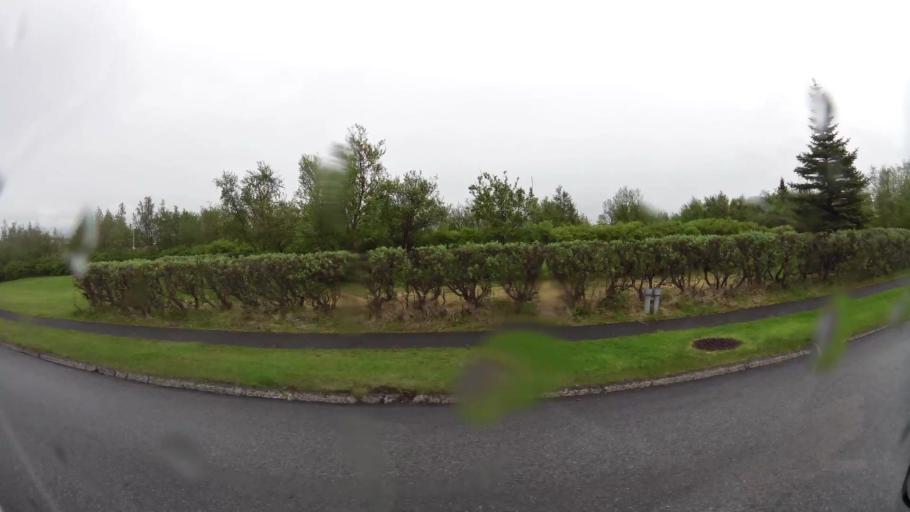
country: IS
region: Capital Region
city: Gardabaer
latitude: 64.0884
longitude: -21.9135
